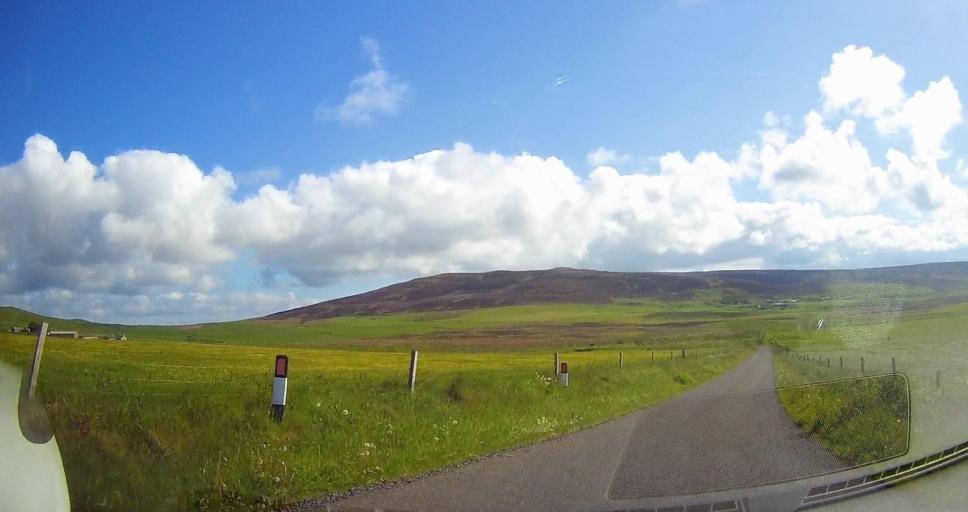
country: GB
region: Scotland
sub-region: Orkney Islands
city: Stromness
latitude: 58.9868
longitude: -3.1469
